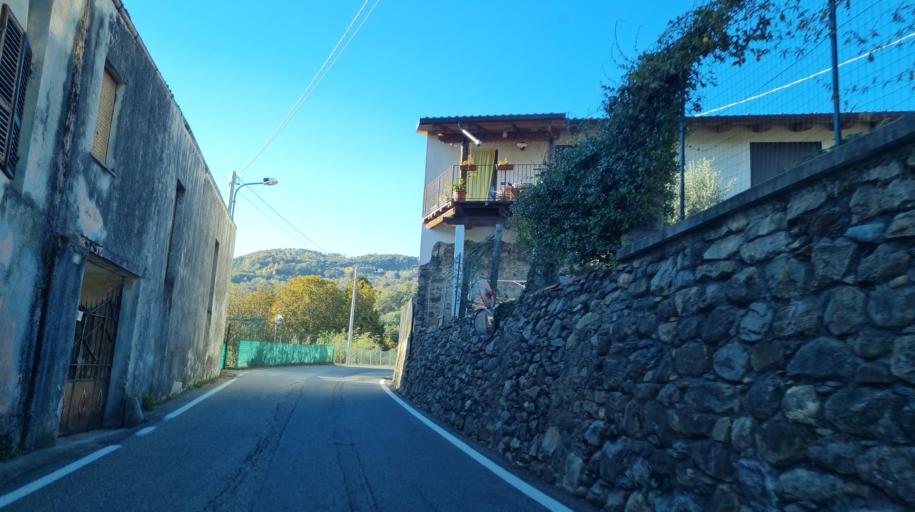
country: IT
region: Piedmont
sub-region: Provincia di Torino
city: Lessolo
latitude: 45.4756
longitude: 7.8100
